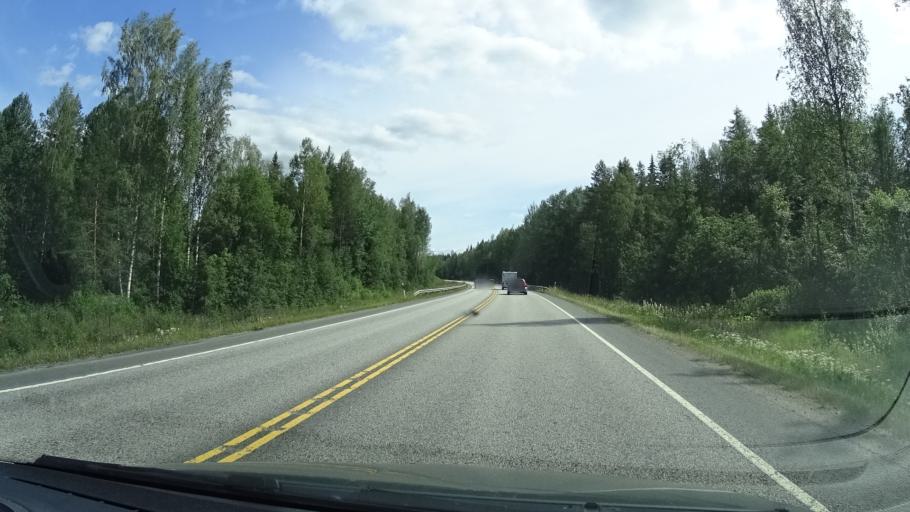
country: FI
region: Central Finland
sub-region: Jyvaeskylae
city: Jyvaeskylae
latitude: 62.2654
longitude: 25.5642
